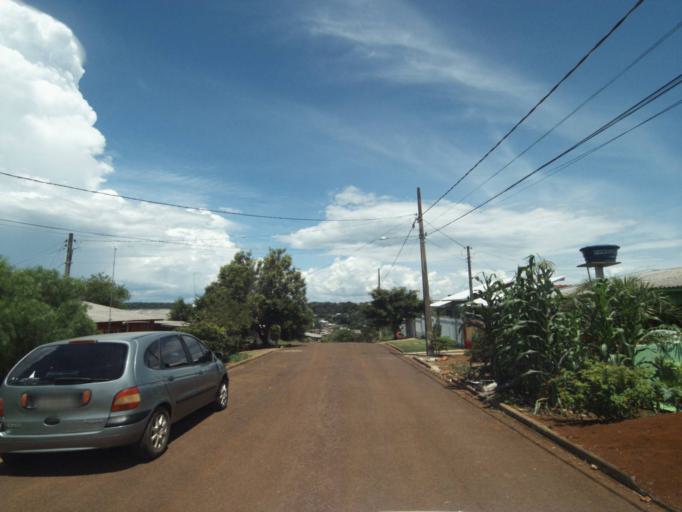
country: BR
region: Parana
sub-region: Guaraniacu
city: Guaraniacu
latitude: -25.0908
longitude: -52.8746
